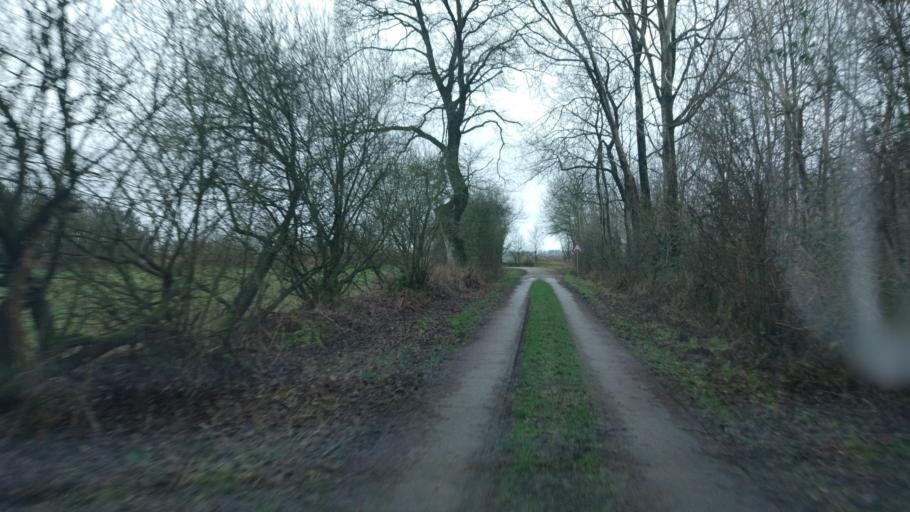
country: DE
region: Schleswig-Holstein
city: Gross Rheide
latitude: 54.4609
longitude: 9.4309
